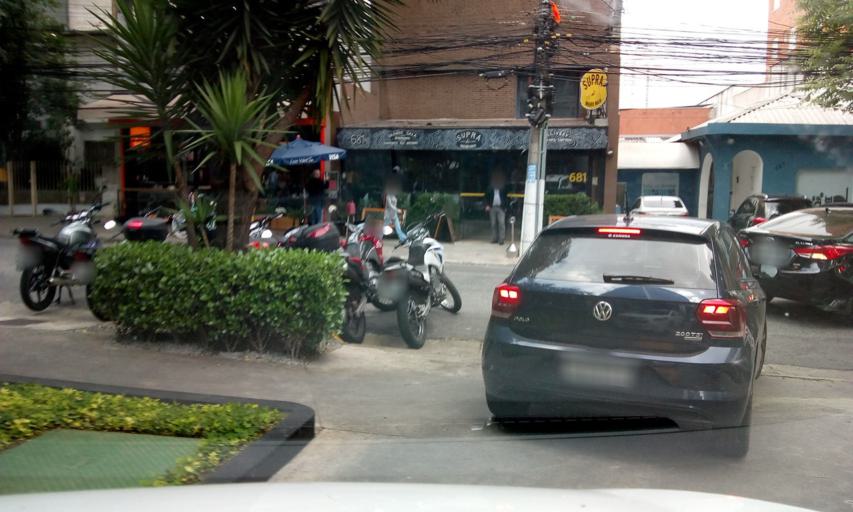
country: BR
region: Sao Paulo
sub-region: Sao Paulo
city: Sao Paulo
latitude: -23.5878
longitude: -46.6795
